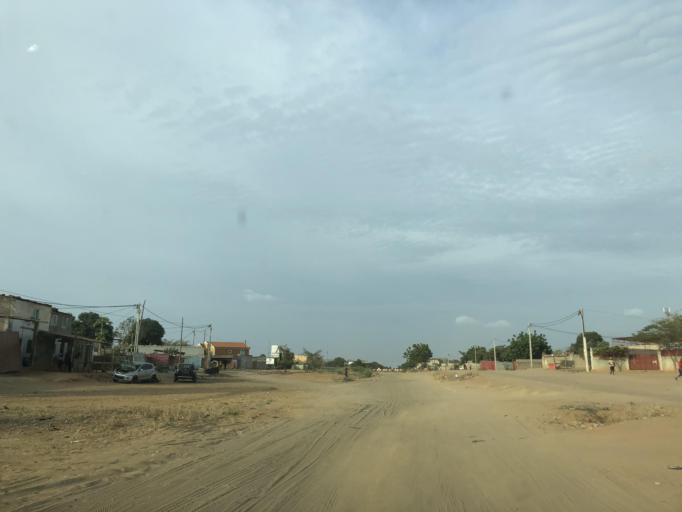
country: AO
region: Luanda
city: Luanda
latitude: -8.9174
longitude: 13.3106
